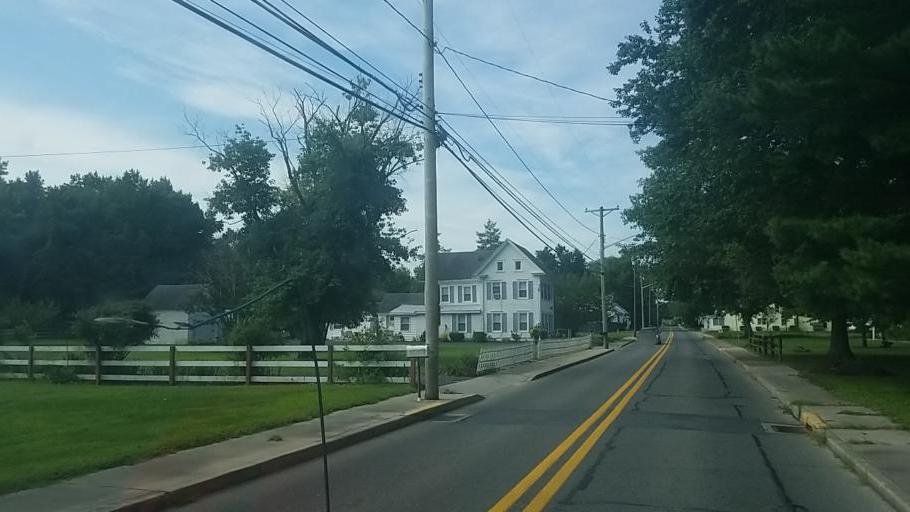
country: US
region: Delaware
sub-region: Sussex County
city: Selbyville
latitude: 38.5194
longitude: -75.2285
